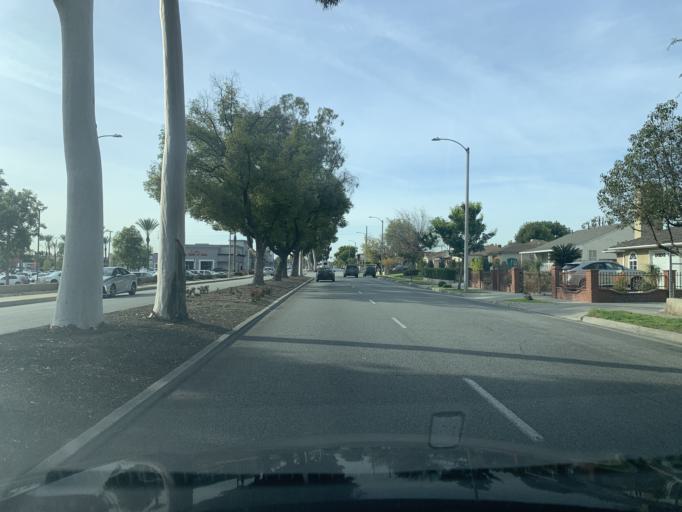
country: US
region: California
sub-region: Los Angeles County
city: Rosemead
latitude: 34.0757
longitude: -118.0701
